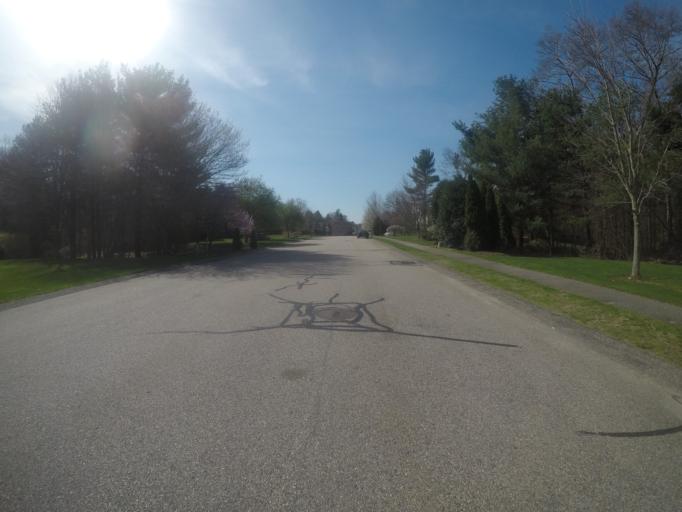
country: US
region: Massachusetts
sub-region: Bristol County
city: Easton
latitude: 42.0174
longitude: -71.1192
